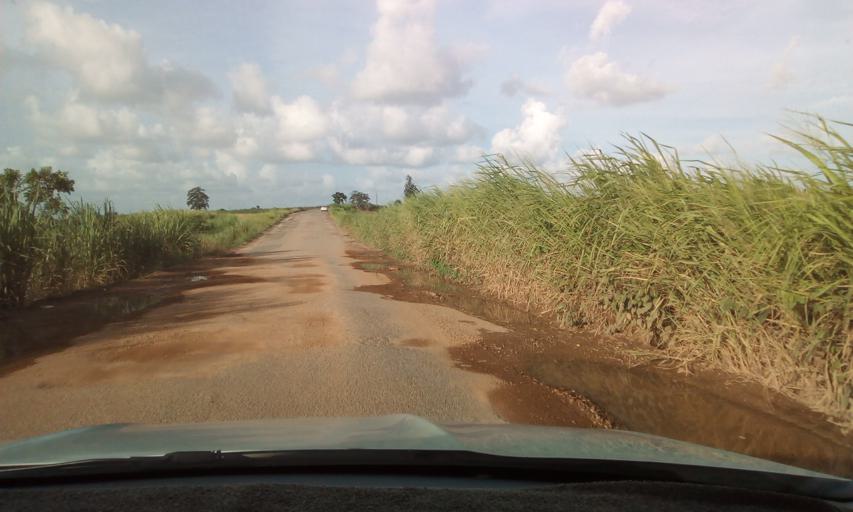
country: BR
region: Pernambuco
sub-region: Gloria Do Goita
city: Gloria do Goita
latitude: -7.9918
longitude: -35.2472
